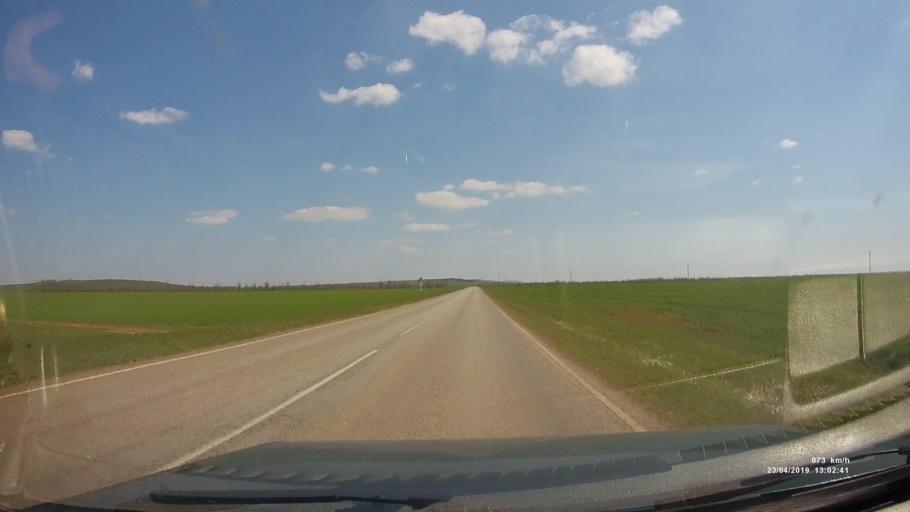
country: RU
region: Kalmykiya
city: Yashalta
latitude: 46.5997
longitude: 42.6727
